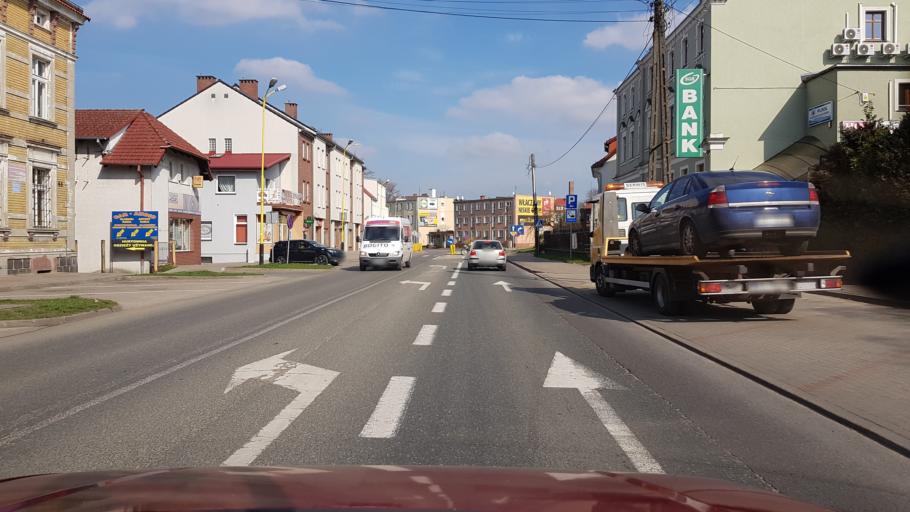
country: PL
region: West Pomeranian Voivodeship
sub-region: Powiat goleniowski
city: Nowogard
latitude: 53.6666
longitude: 15.1187
